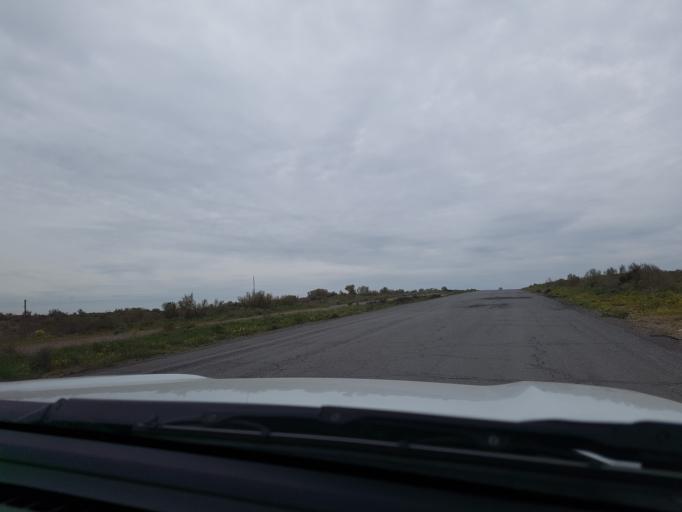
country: TM
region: Mary
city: Bayramaly
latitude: 37.8867
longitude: 62.6146
